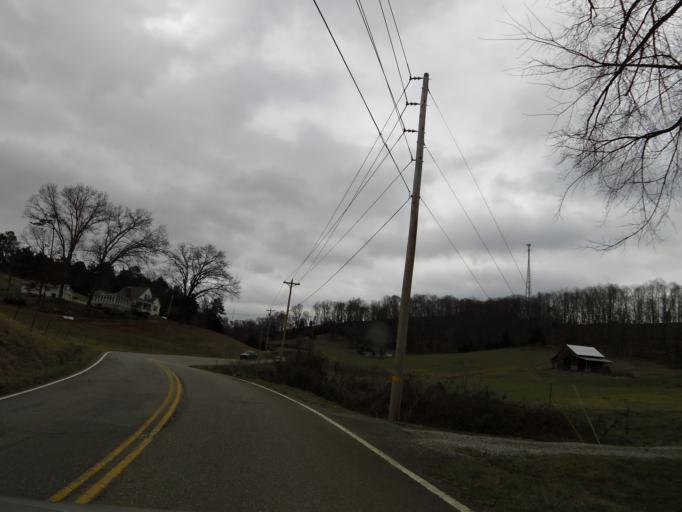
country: US
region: Tennessee
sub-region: Jefferson County
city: Jefferson City
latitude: 36.1876
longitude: -83.5147
